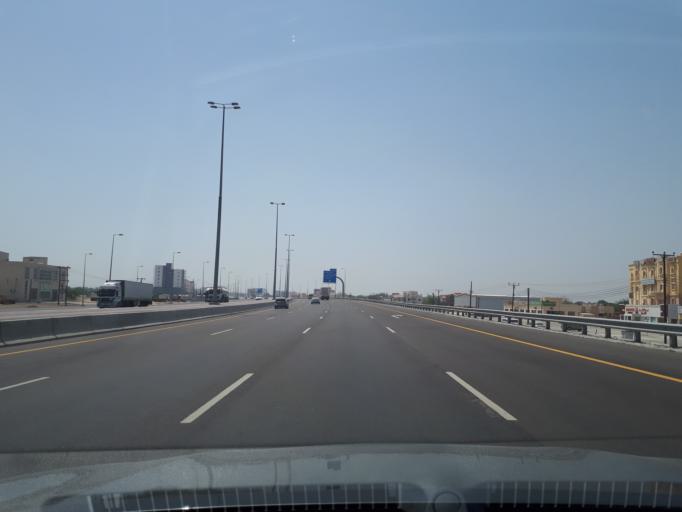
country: OM
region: Al Batinah
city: Al Sohar
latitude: 24.4180
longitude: 56.6264
